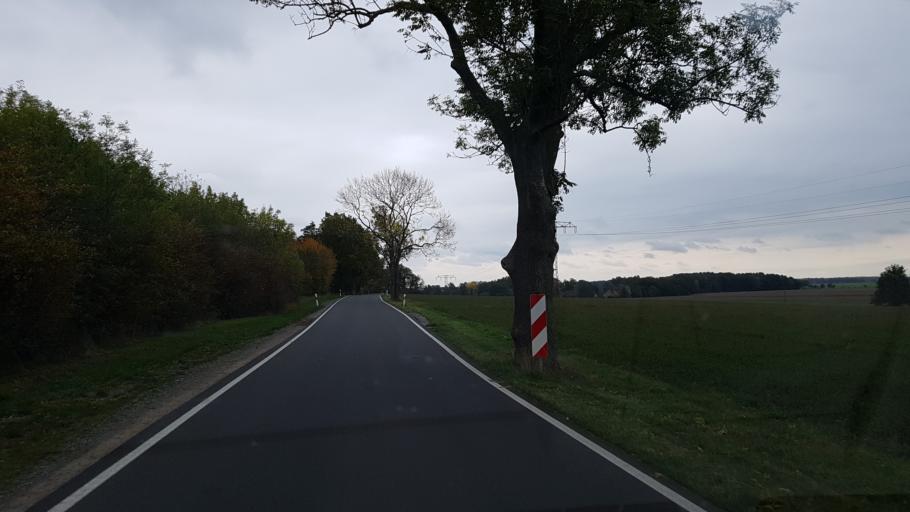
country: DE
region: Saxony
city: Falkenhain
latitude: 51.3841
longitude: 12.9002
